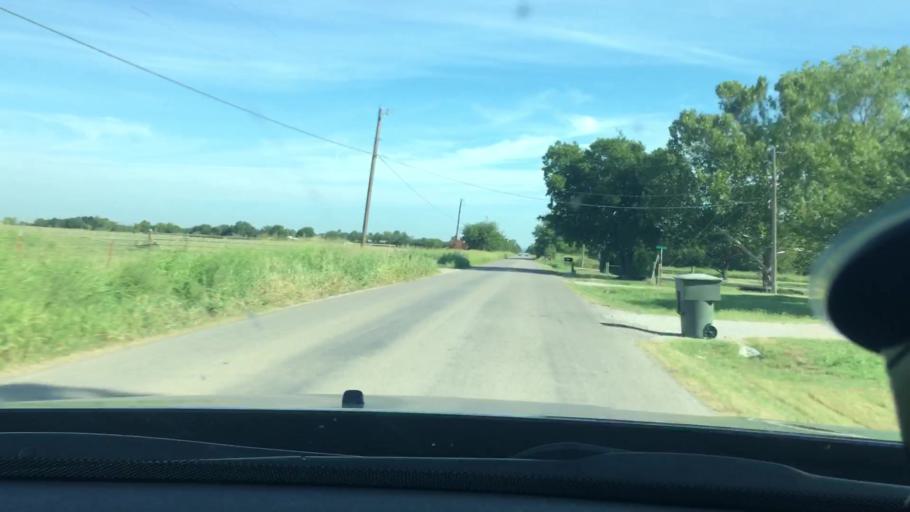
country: US
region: Oklahoma
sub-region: Carter County
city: Lone Grove
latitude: 34.1924
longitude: -97.2475
